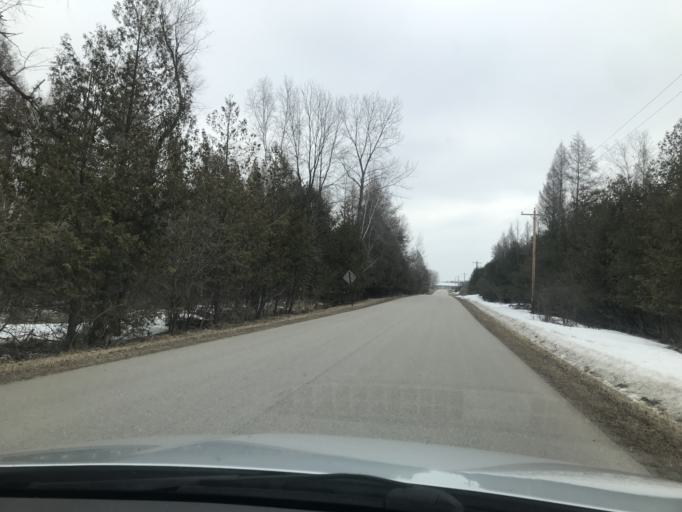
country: US
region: Wisconsin
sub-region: Marinette County
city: Peshtigo
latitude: 45.0274
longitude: -87.8674
